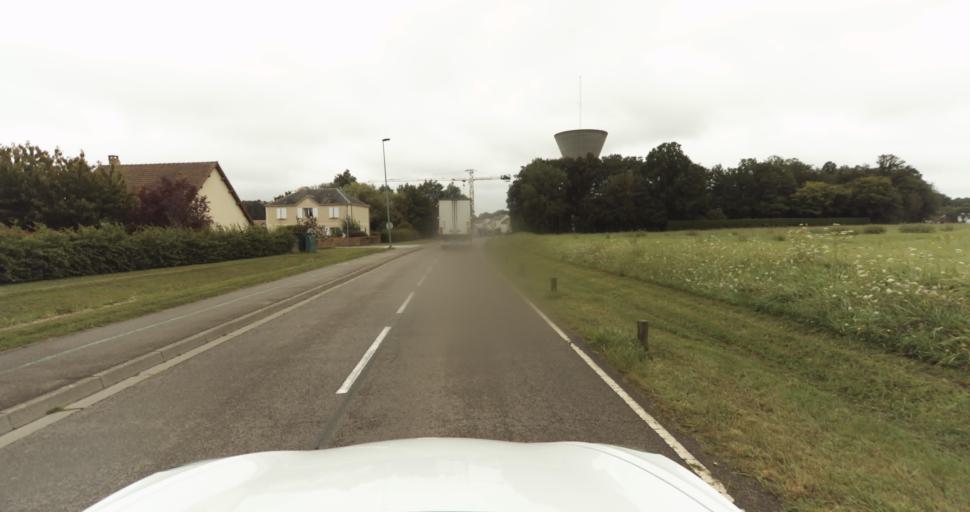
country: FR
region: Haute-Normandie
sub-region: Departement de l'Eure
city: Aviron
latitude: 49.0422
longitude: 1.1292
